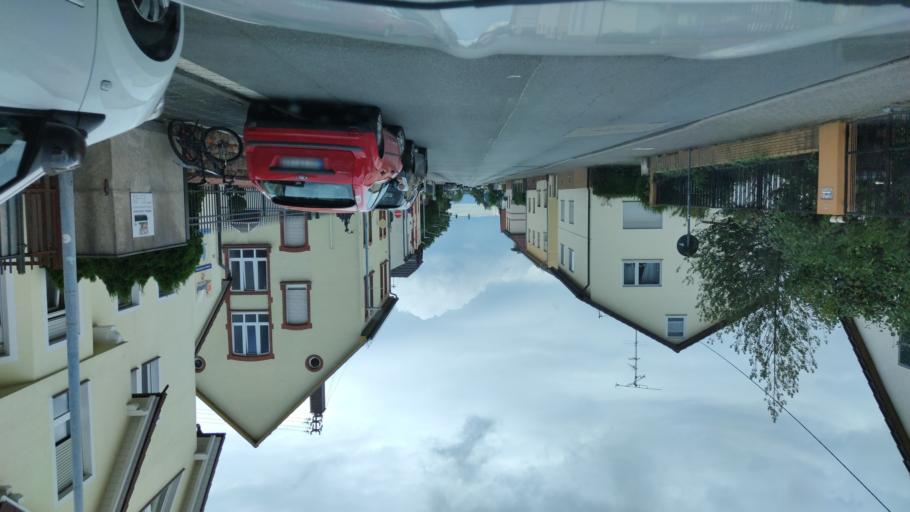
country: DE
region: Hesse
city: Dreieich
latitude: 50.0011
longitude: 8.7106
